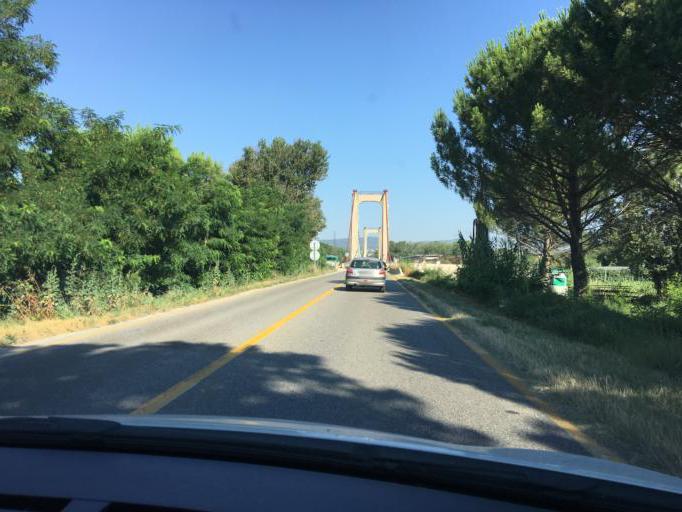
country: FR
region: Provence-Alpes-Cote d'Azur
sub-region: Departement des Alpes-de-Haute-Provence
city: Manosque
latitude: 43.8030
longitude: 5.8277
